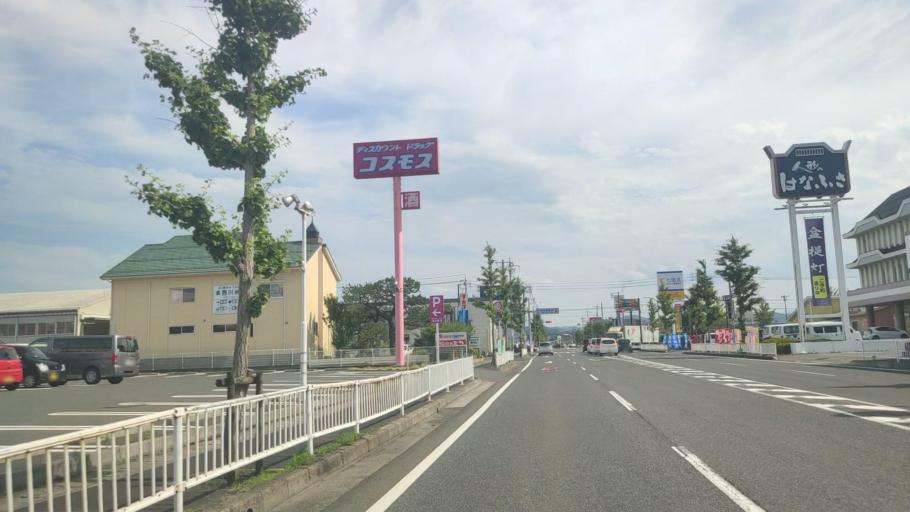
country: JP
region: Tottori
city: Tottori
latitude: 35.5182
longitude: 134.1922
